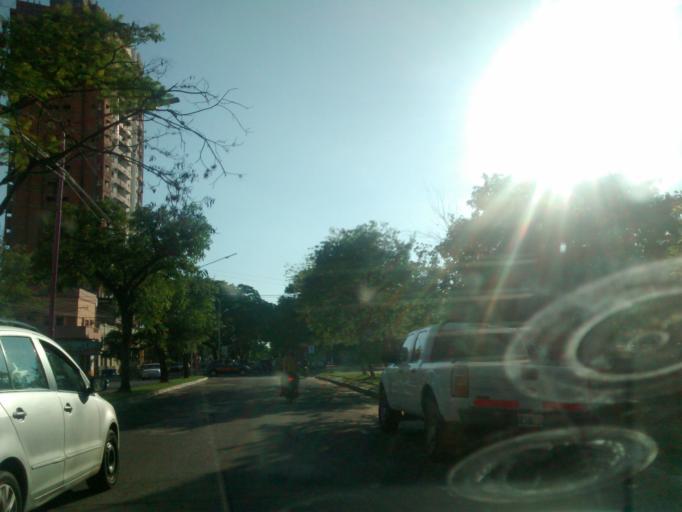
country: AR
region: Chaco
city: Resistencia
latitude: -27.4577
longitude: -58.9851
